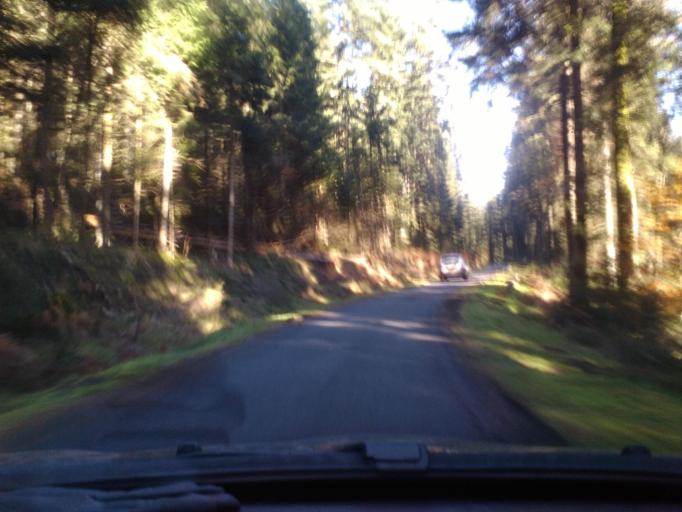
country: FR
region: Alsace
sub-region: Departement du Bas-Rhin
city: Rothau
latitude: 48.4723
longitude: 7.0836
